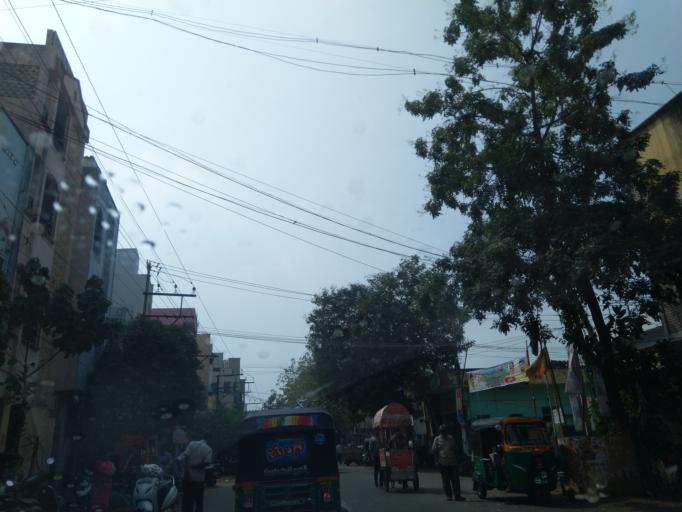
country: IN
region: Andhra Pradesh
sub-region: Krishna
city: Vijayawada
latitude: 16.5219
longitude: 80.6034
